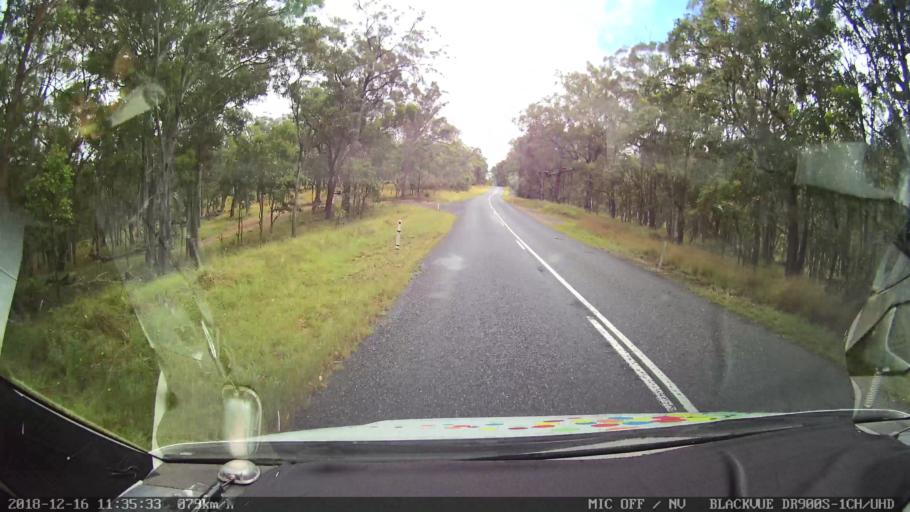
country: AU
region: New South Wales
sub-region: Tenterfield Municipality
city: Carrolls Creek
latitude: -28.9888
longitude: 152.1634
